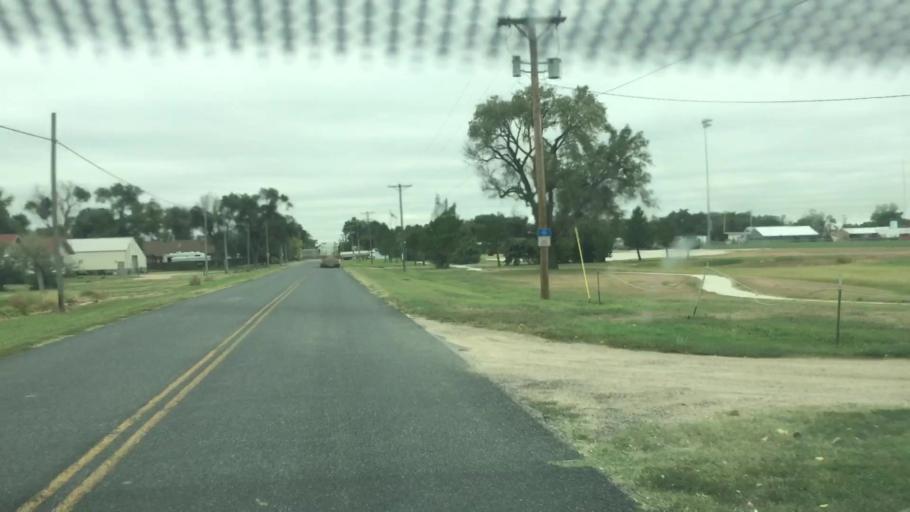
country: US
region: Kansas
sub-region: Hamilton County
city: Syracuse
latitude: 38.0564
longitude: -102.1186
